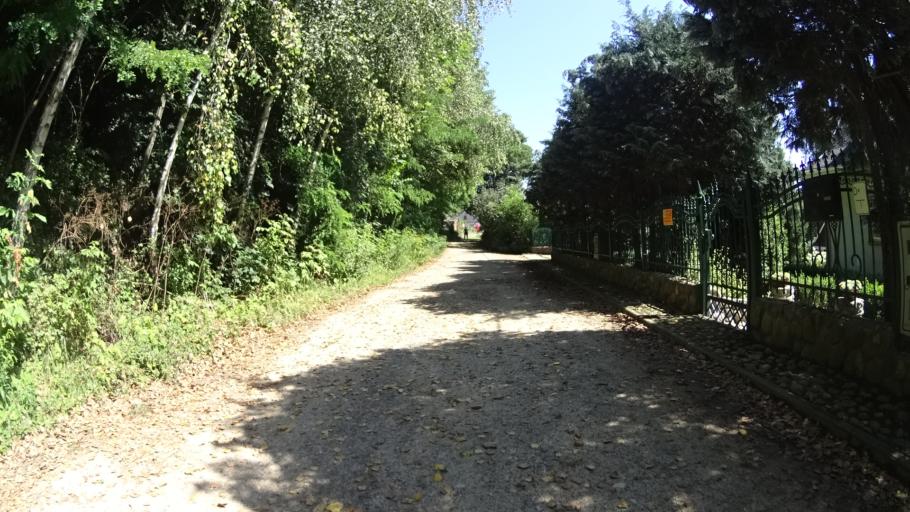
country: PL
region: Masovian Voivodeship
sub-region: Powiat bialobrzeski
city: Bialobrzegi
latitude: 51.6664
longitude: 20.8840
